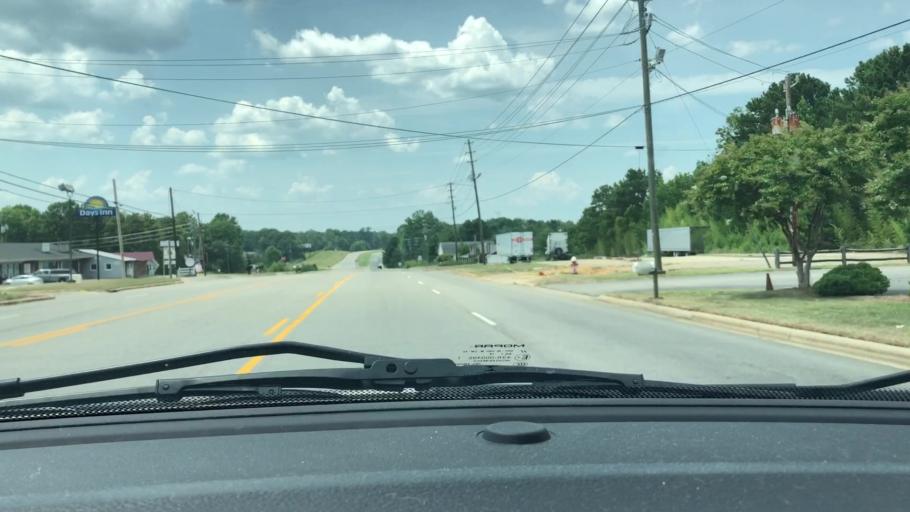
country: US
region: North Carolina
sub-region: Lee County
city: Sanford
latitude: 35.4972
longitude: -79.1981
